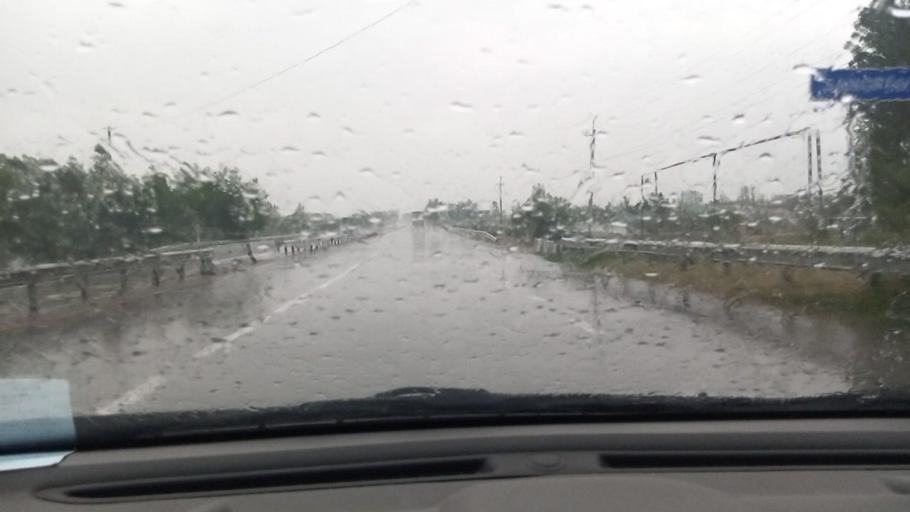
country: UZ
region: Toshkent Shahri
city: Bektemir
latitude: 41.1526
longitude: 69.4259
